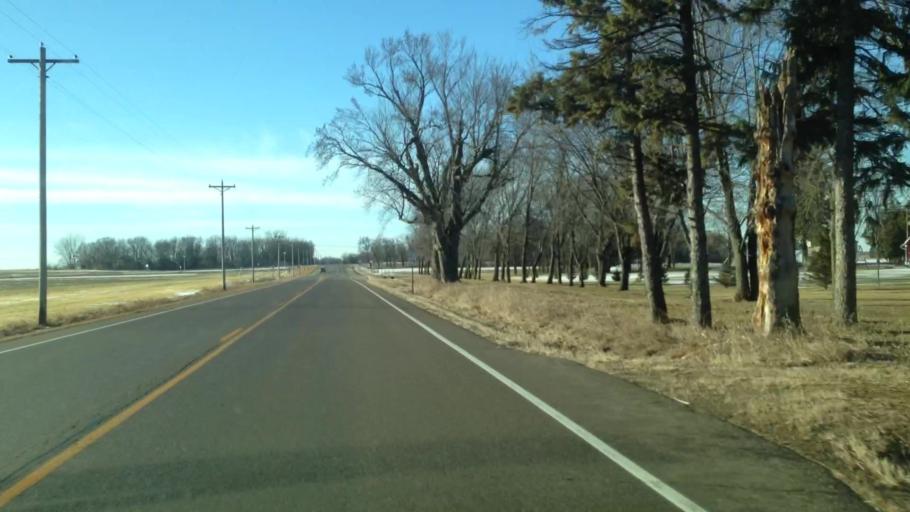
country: US
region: Minnesota
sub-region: Dakota County
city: Farmington
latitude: 44.5479
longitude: -93.0534
